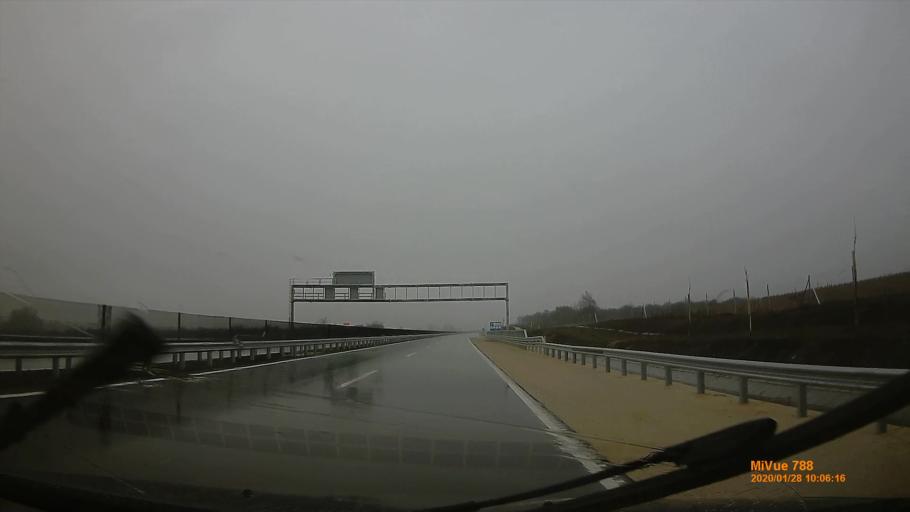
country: HU
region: Pest
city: Pilis
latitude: 47.2832
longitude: 19.5872
